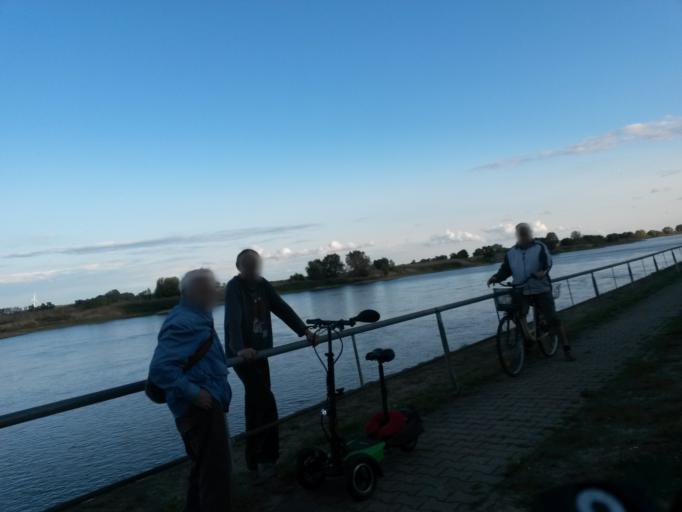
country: DE
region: Saxony-Anhalt
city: Tangermunde
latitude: 52.5488
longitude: 11.9828
